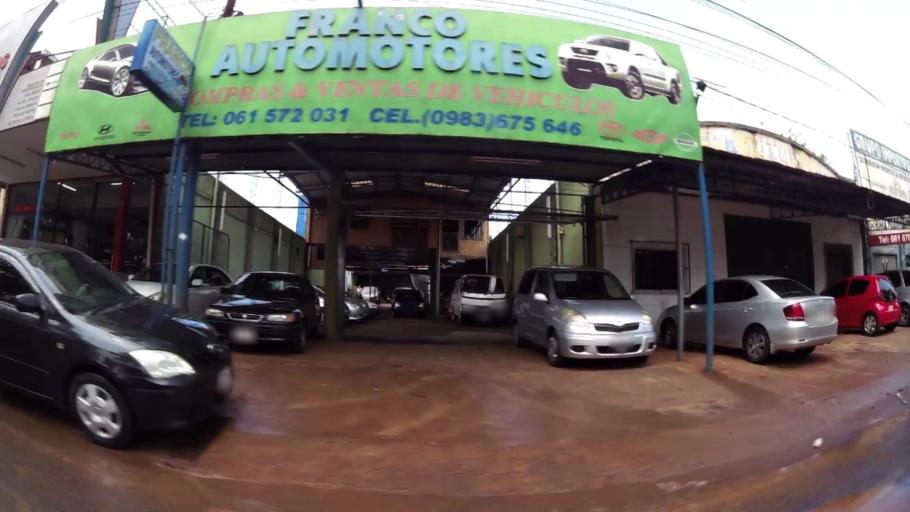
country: PY
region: Alto Parana
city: Ciudad del Este
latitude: -25.5006
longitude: -54.6591
